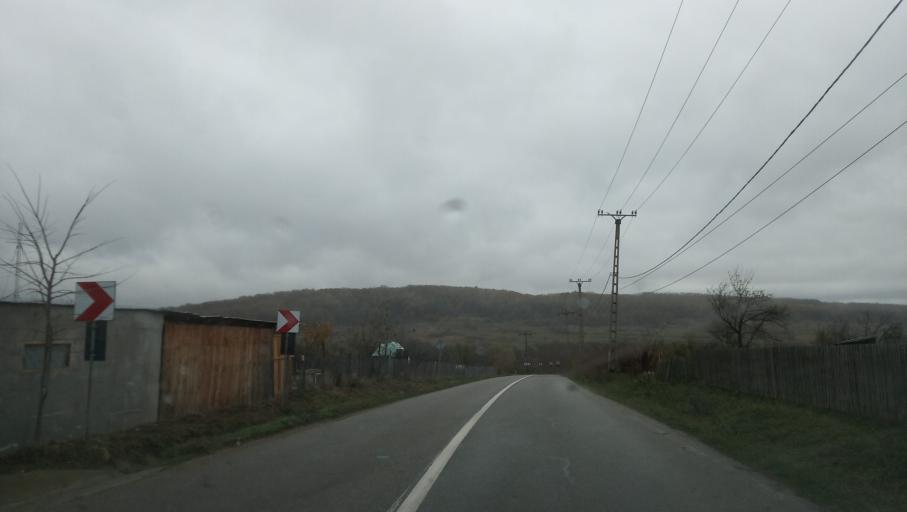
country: RO
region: Gorj
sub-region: Comuna Musetesti
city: Musetesti
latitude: 45.1507
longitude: 23.4594
